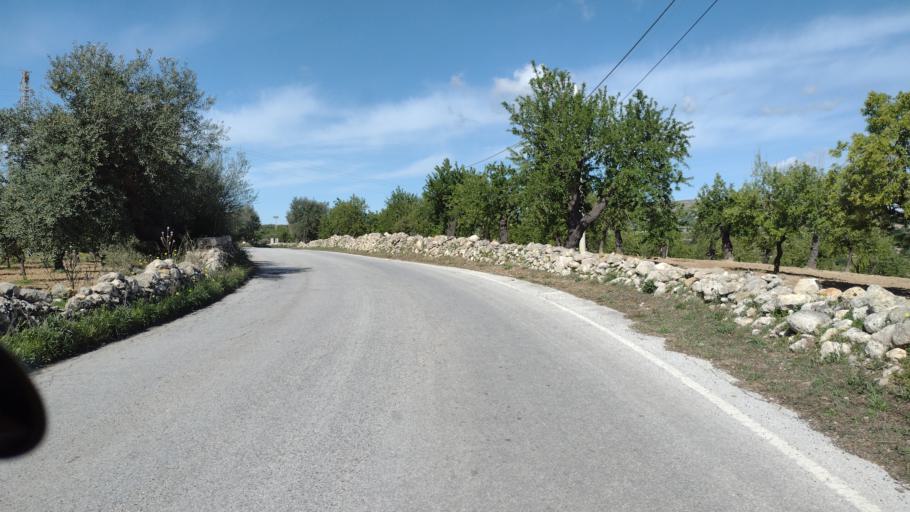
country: IT
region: Sicily
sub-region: Provincia di Siracusa
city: Noto
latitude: 36.8884
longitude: 15.0500
